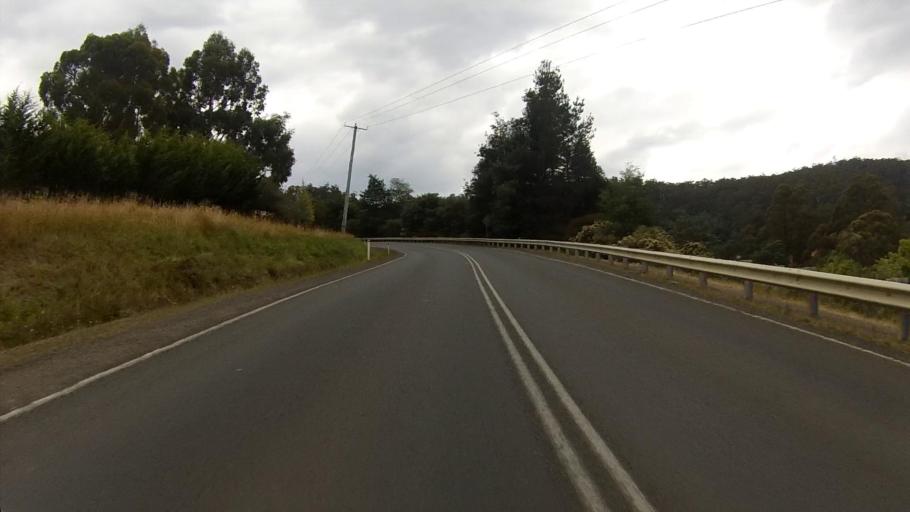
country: AU
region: Tasmania
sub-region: Huon Valley
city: Cygnet
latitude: -43.1298
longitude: 147.0474
